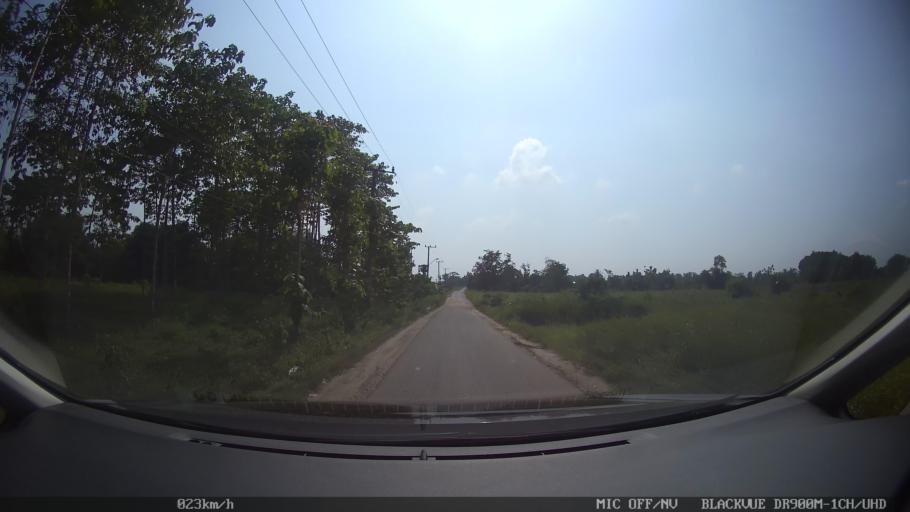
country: ID
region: Lampung
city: Natar
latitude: -5.2653
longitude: 105.2019
